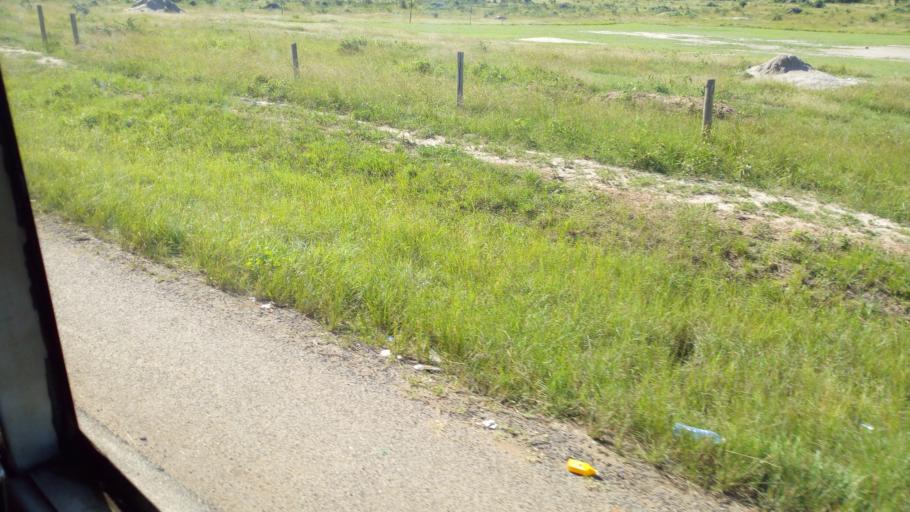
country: UG
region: Central Region
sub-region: Lyantonde District
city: Lyantonde
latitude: -0.4615
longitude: 31.0397
